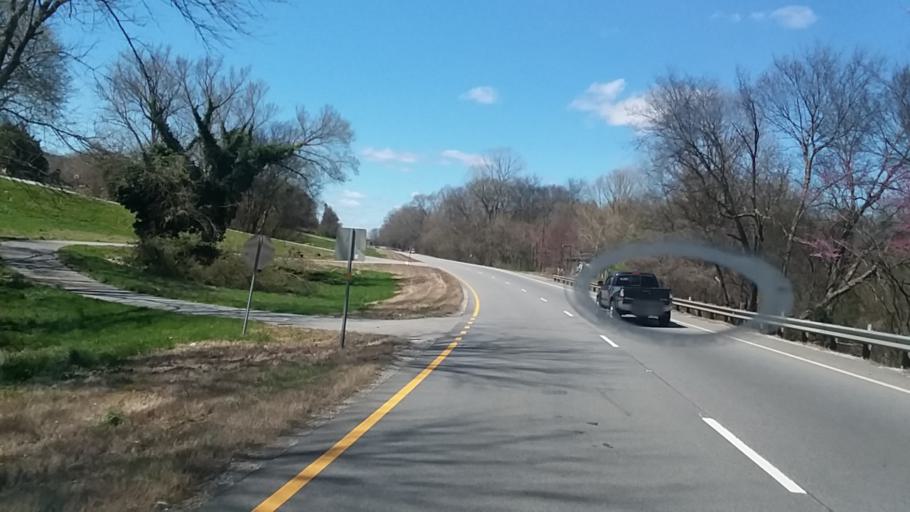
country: US
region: Alabama
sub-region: Colbert County
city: Tuscumbia
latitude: 34.7149
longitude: -87.7798
